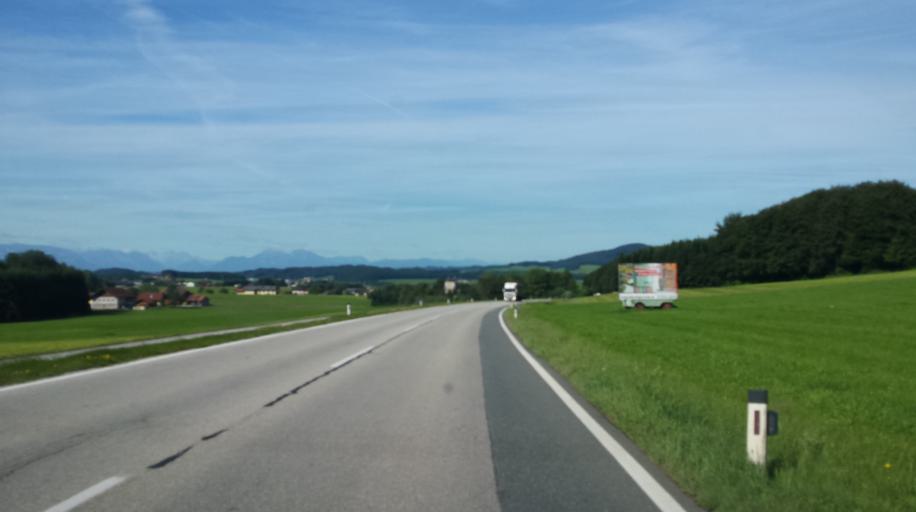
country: AT
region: Salzburg
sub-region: Politischer Bezirk Salzburg-Umgebung
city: Strasswalchen
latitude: 47.9878
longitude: 13.2822
